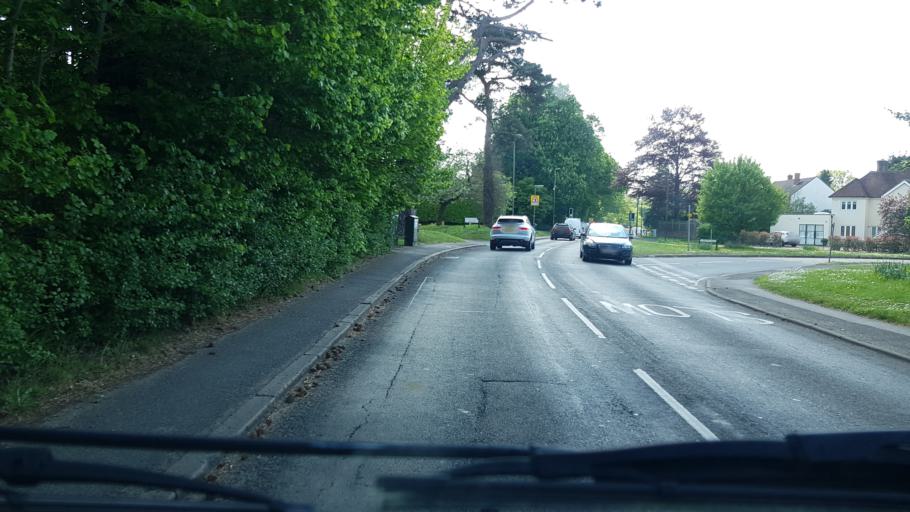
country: GB
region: England
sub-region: Surrey
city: Cobham
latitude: 51.3223
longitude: -0.3875
